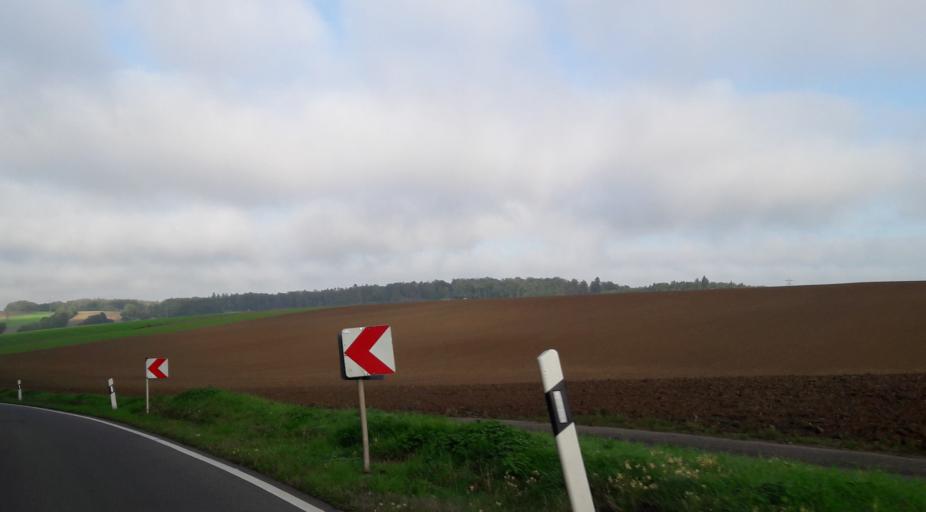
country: DE
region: Baden-Wuerttemberg
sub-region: Regierungsbezirk Stuttgart
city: Kirchardt
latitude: 49.2128
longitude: 8.9836
